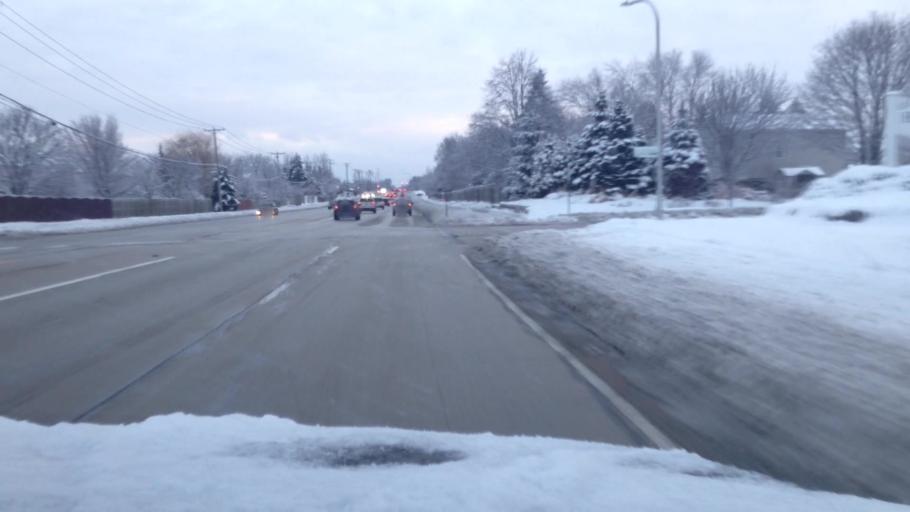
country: US
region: Illinois
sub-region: Kane County
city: South Elgin
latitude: 42.0031
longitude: -88.3156
